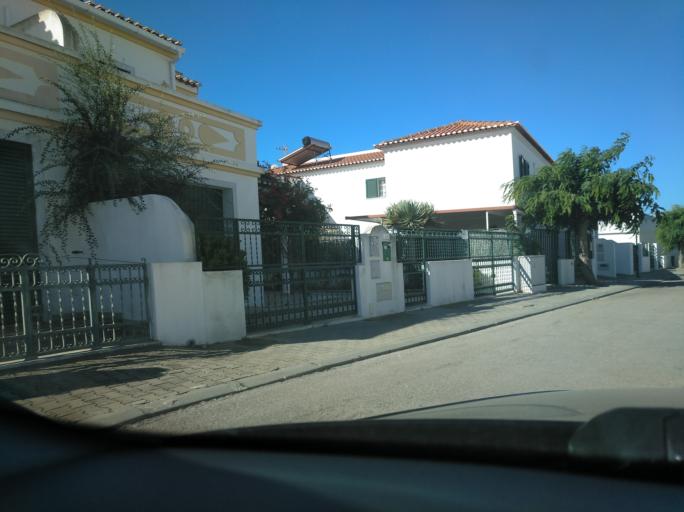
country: PT
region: Faro
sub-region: Vila Real de Santo Antonio
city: Monte Gordo
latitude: 37.1702
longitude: -7.5140
